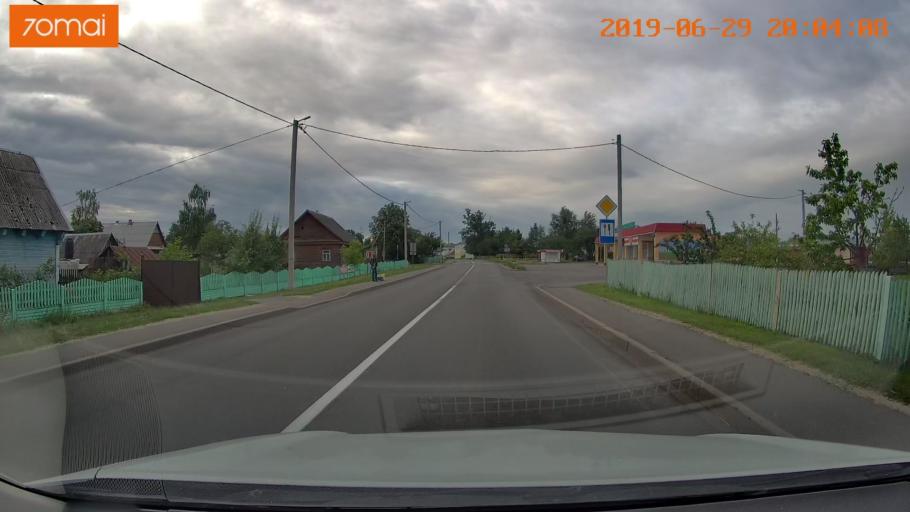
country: BY
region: Brest
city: Lahishyn
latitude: 52.3342
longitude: 25.9903
